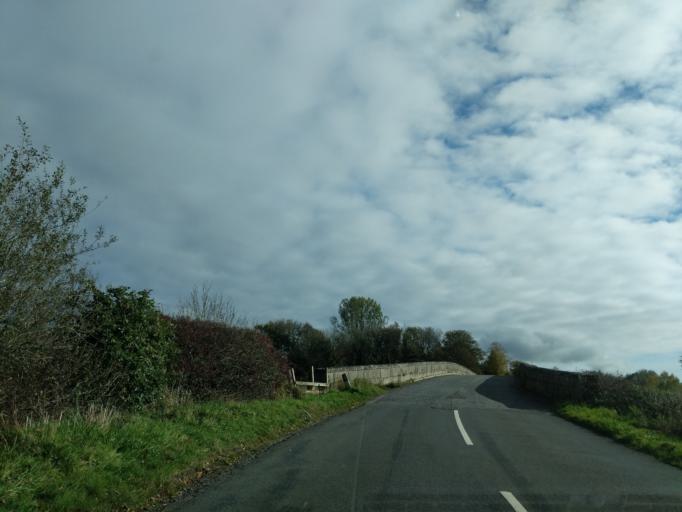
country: GB
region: Scotland
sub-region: Dumfries and Galloway
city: Castle Douglas
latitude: 55.0811
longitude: -4.1327
